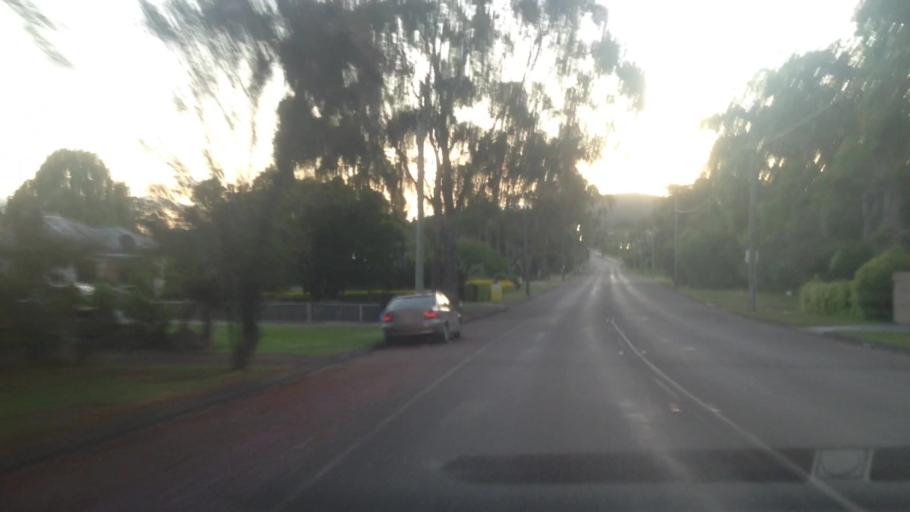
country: AU
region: New South Wales
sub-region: Lake Macquarie Shire
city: Cooranbong
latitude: -33.0715
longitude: 151.4617
